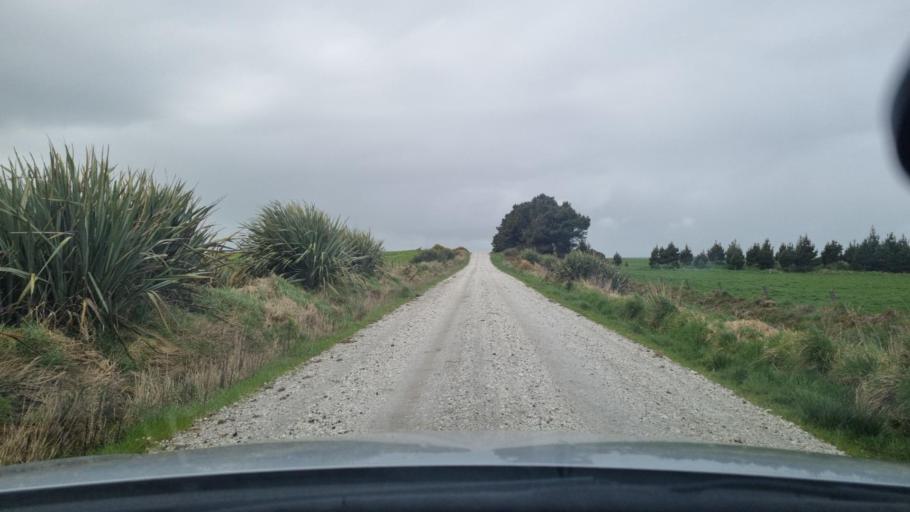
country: NZ
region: Southland
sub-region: Invercargill City
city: Invercargill
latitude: -46.5022
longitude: 168.4060
